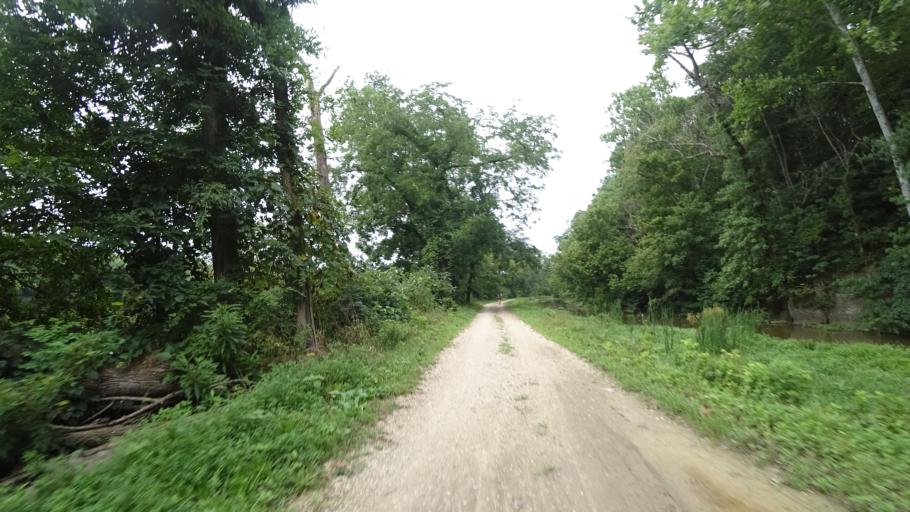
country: US
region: Maryland
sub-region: Montgomery County
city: Travilah
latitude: 39.0405
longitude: -77.2629
